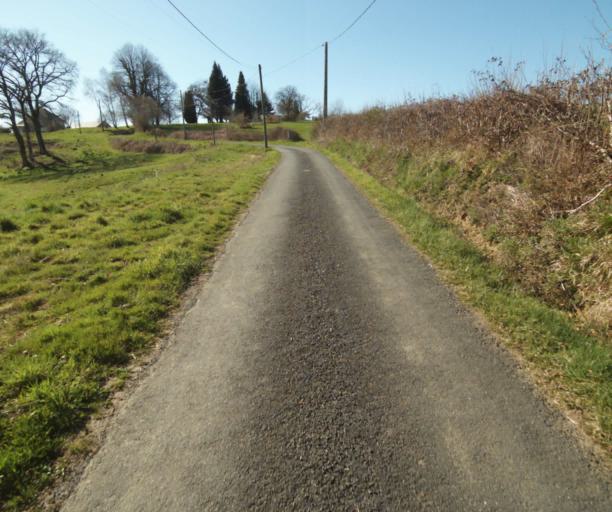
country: FR
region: Limousin
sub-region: Departement de la Correze
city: Uzerche
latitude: 45.4259
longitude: 1.6261
